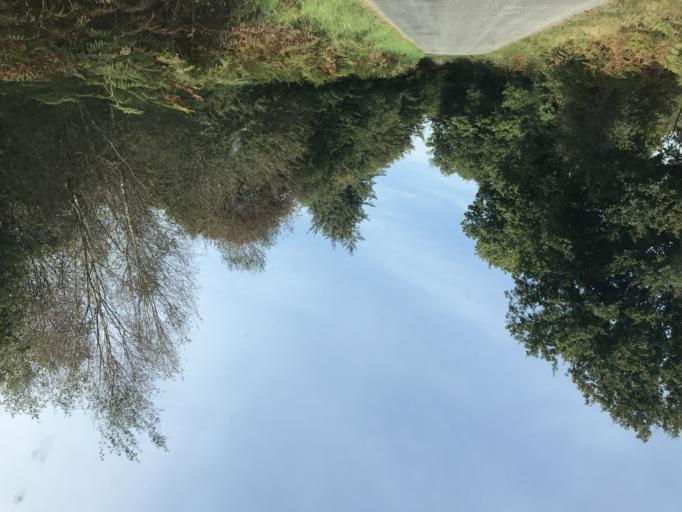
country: FR
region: Brittany
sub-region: Departement du Finistere
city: Brasparts
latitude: 48.3395
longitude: -3.8994
